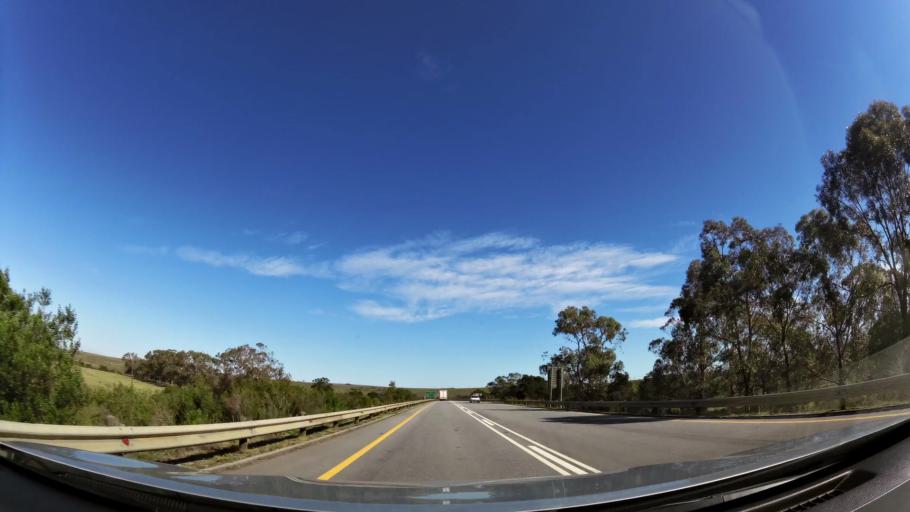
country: ZA
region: Eastern Cape
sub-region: Cacadu District Municipality
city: Kruisfontein
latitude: -34.0355
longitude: 24.5924
